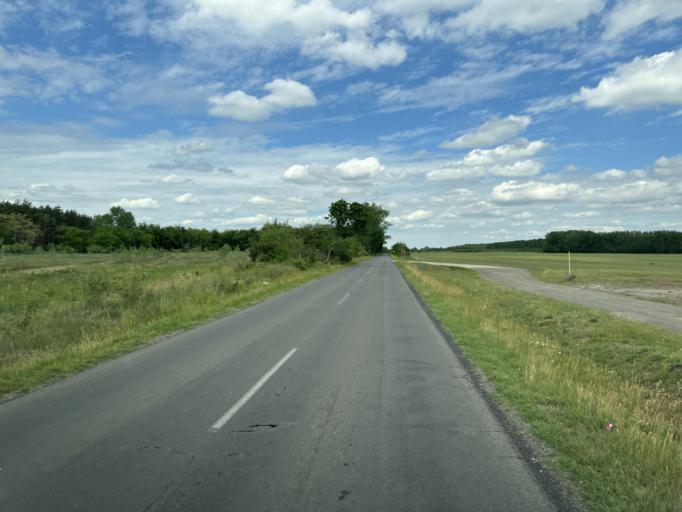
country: HU
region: Pest
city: Toalmas
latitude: 47.4851
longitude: 19.6875
